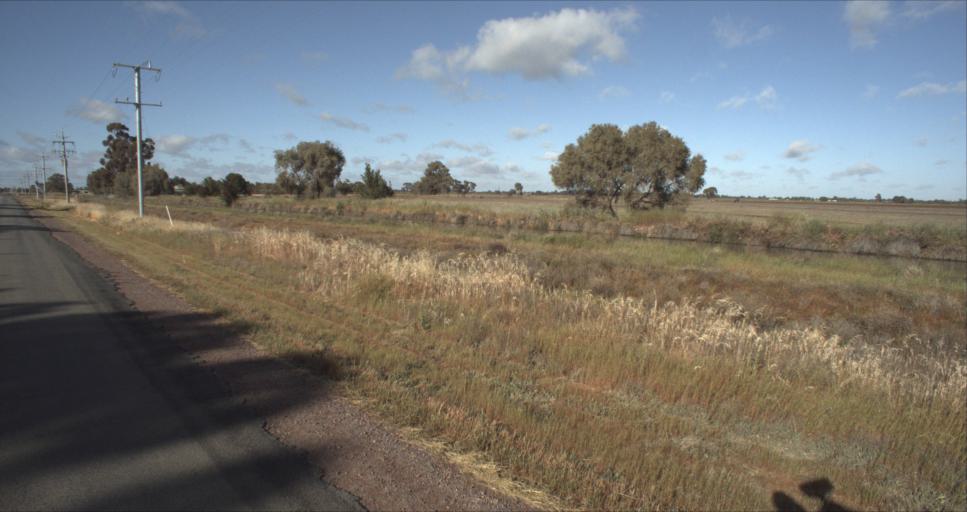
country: AU
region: New South Wales
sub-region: Leeton
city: Leeton
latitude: -34.5291
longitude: 146.3891
